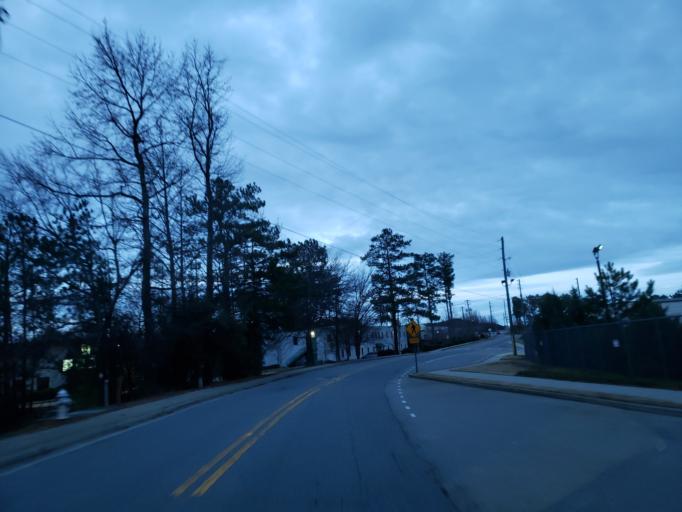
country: US
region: Georgia
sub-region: Cobb County
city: Kennesaw
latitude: 34.0210
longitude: -84.5964
